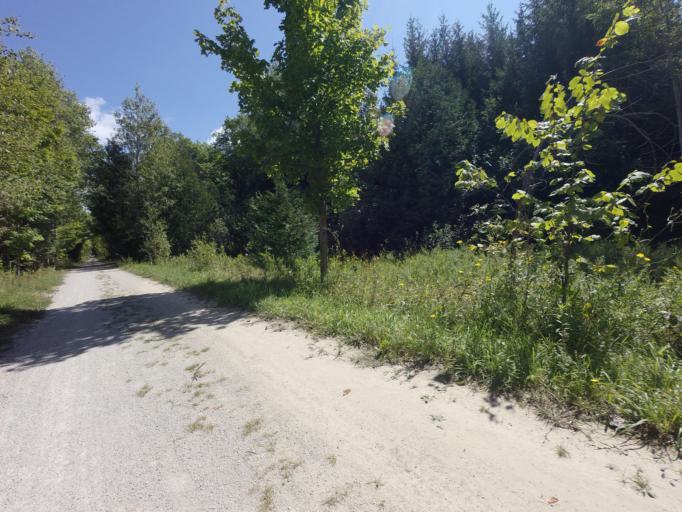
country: CA
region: Ontario
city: Orangeville
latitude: 43.7761
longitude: -80.1086
